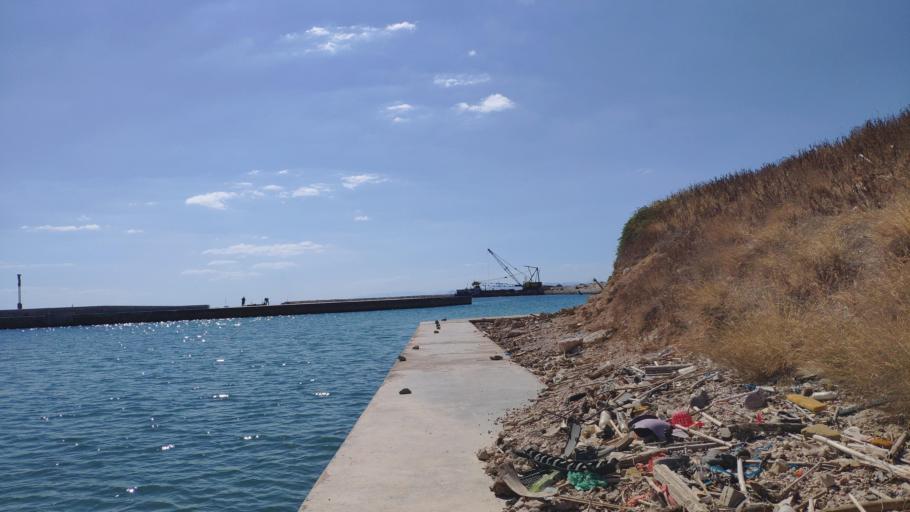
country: GR
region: Attica
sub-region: Nomarchia Athinas
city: Moskhaton
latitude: 37.9426
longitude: 23.6733
